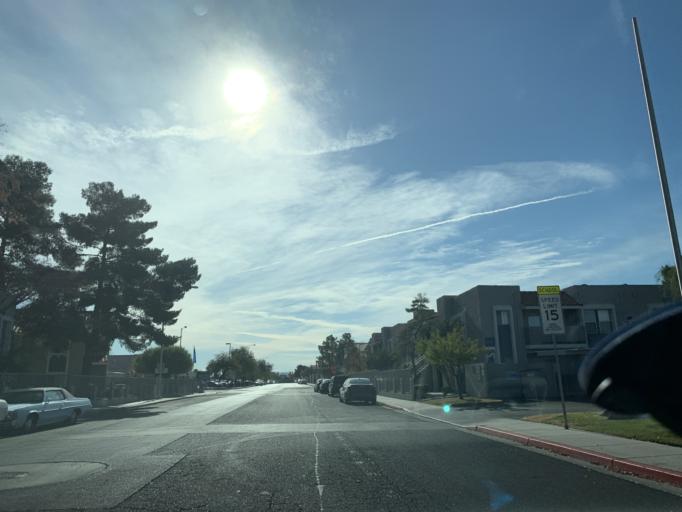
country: US
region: Nevada
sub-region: Clark County
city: Spring Valley
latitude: 36.0974
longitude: -115.2209
